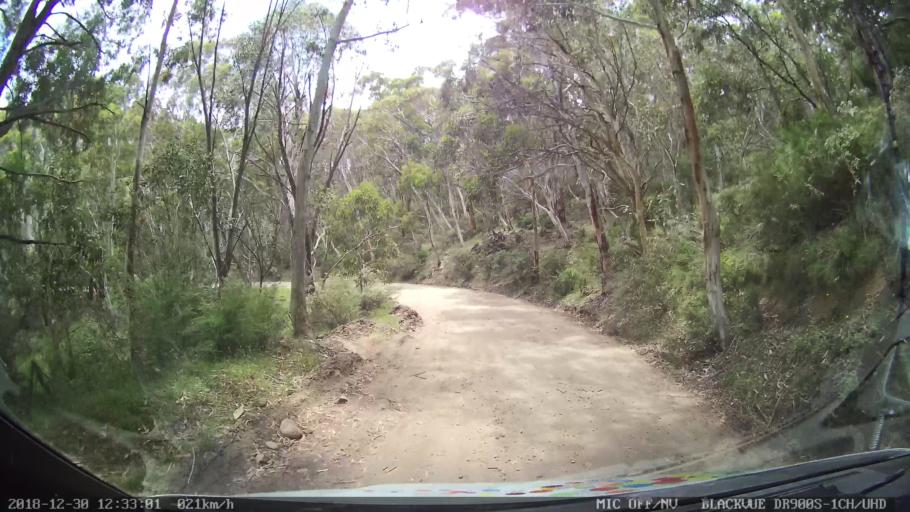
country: AU
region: New South Wales
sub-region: Snowy River
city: Jindabyne
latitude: -36.3242
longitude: 148.4675
